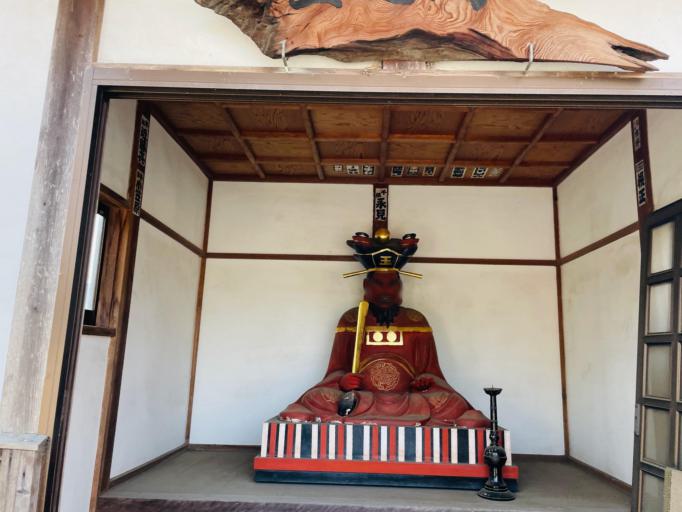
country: JP
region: Saitama
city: Ogawa
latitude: 36.1014
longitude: 139.2696
